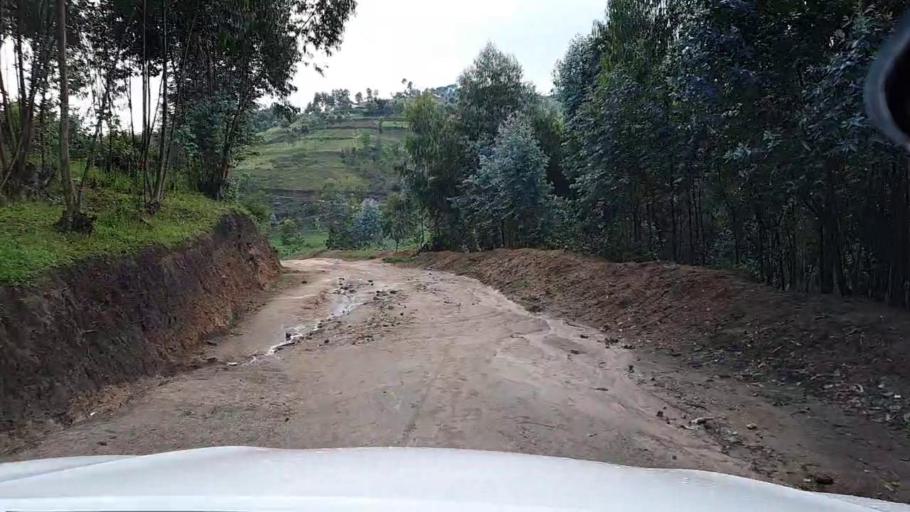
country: BI
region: Kayanza
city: Kayanza
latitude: -2.7719
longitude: 29.4463
